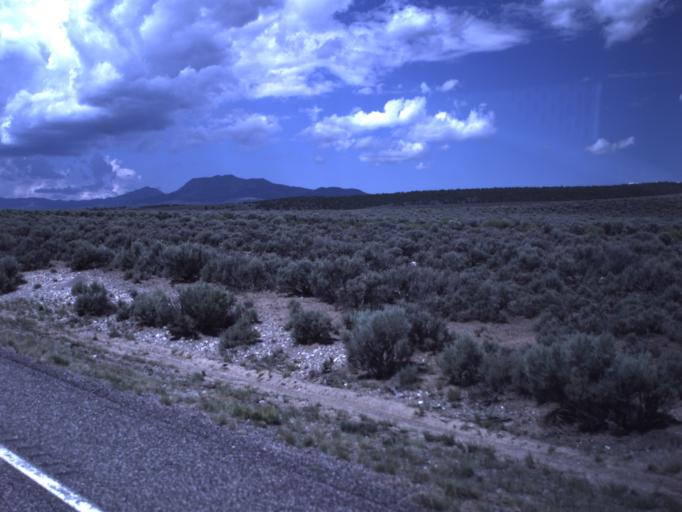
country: US
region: Utah
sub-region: Garfield County
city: Panguitch
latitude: 37.9850
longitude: -112.3975
